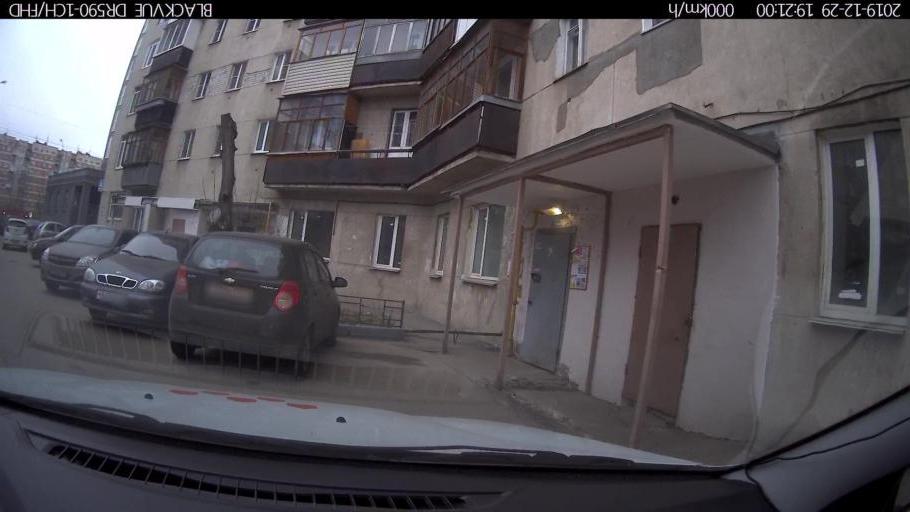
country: RU
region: Nizjnij Novgorod
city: Nizhniy Novgorod
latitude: 56.3273
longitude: 43.8729
